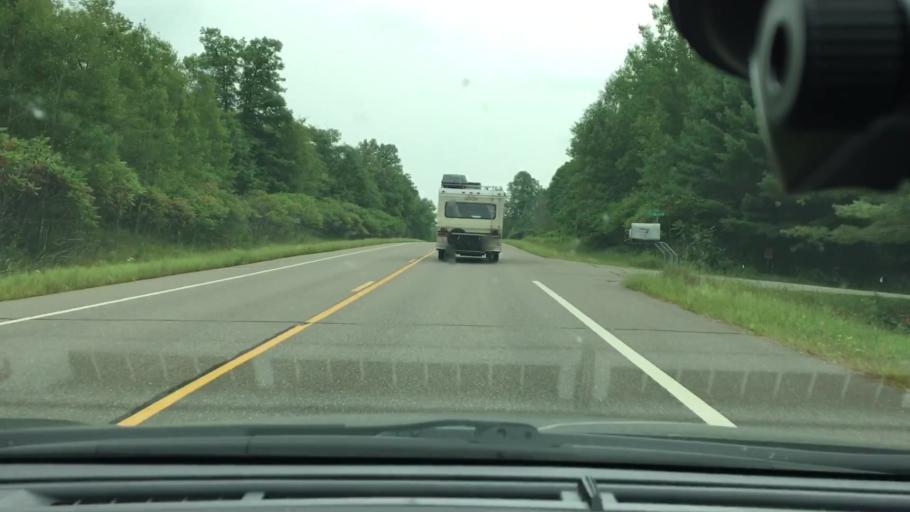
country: US
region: Minnesota
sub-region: Crow Wing County
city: Crosby
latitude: 46.4074
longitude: -93.8161
